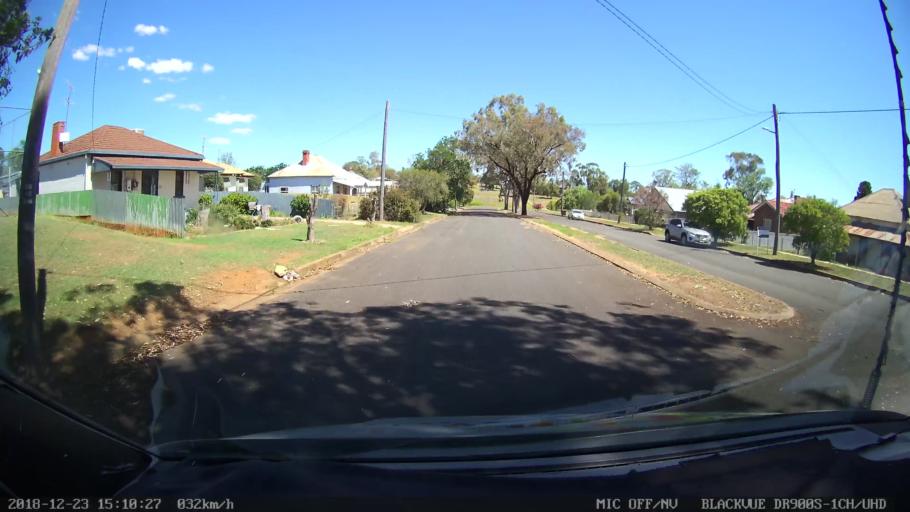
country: AU
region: New South Wales
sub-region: Tamworth Municipality
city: Manilla
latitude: -30.7504
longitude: 150.7215
